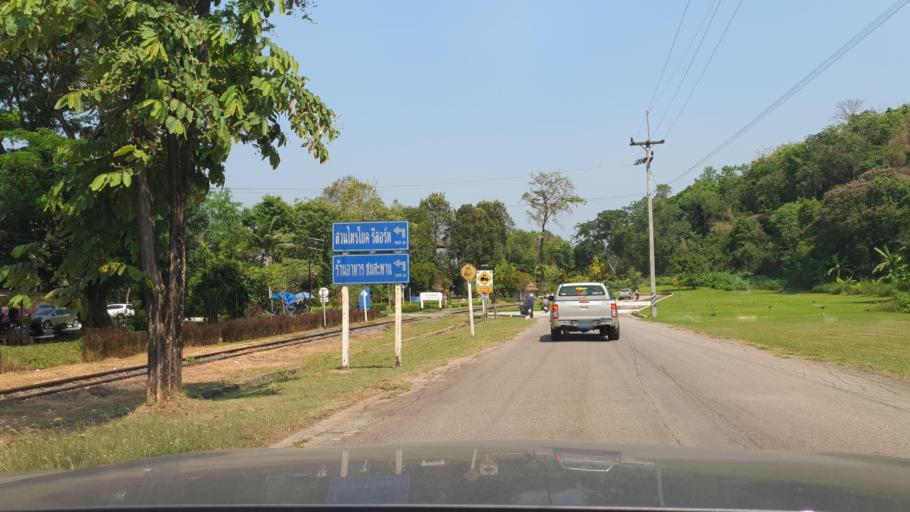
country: TH
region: Kanchanaburi
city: Sai Yok
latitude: 14.0993
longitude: 99.1705
